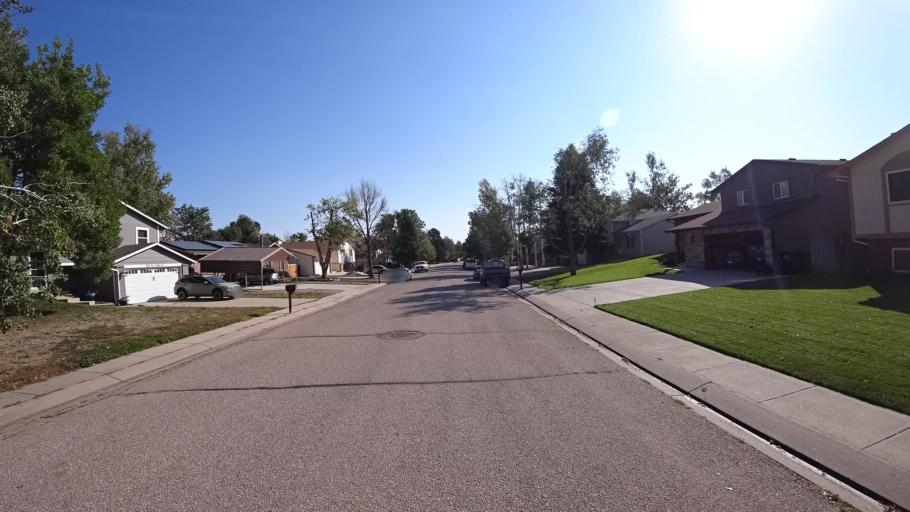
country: US
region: Colorado
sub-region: El Paso County
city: Cimarron Hills
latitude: 38.8829
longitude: -104.7253
